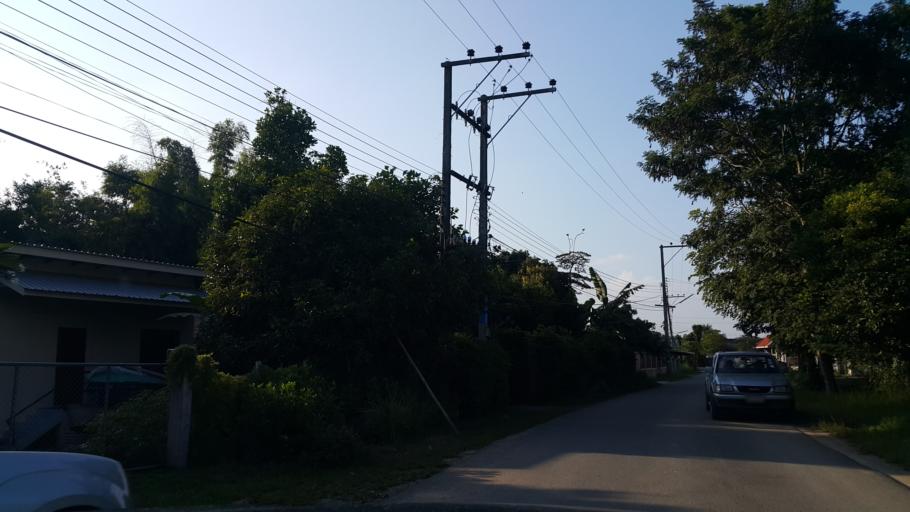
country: TH
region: Chiang Mai
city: San Sai
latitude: 18.9425
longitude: 98.9222
